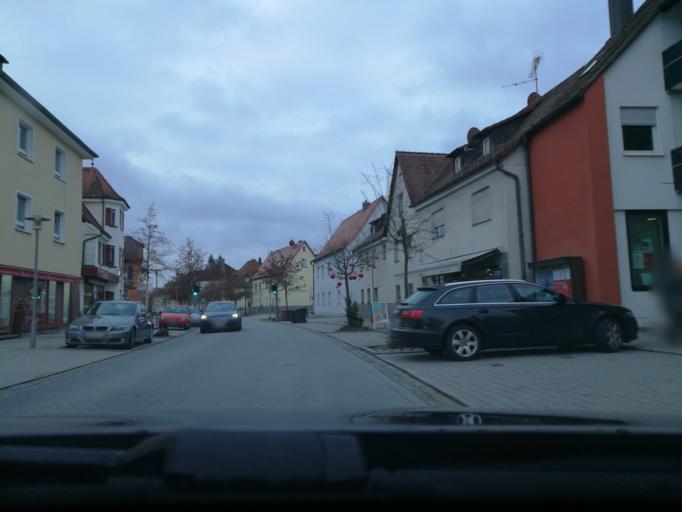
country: DE
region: Bavaria
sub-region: Regierungsbezirk Mittelfranken
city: Heroldsberg
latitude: 49.5308
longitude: 11.1511
